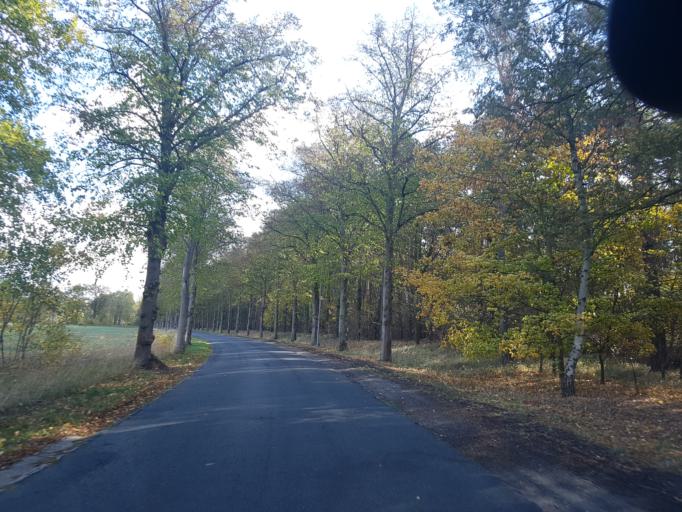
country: DE
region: Brandenburg
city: Nauen
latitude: 52.6604
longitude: 12.9176
